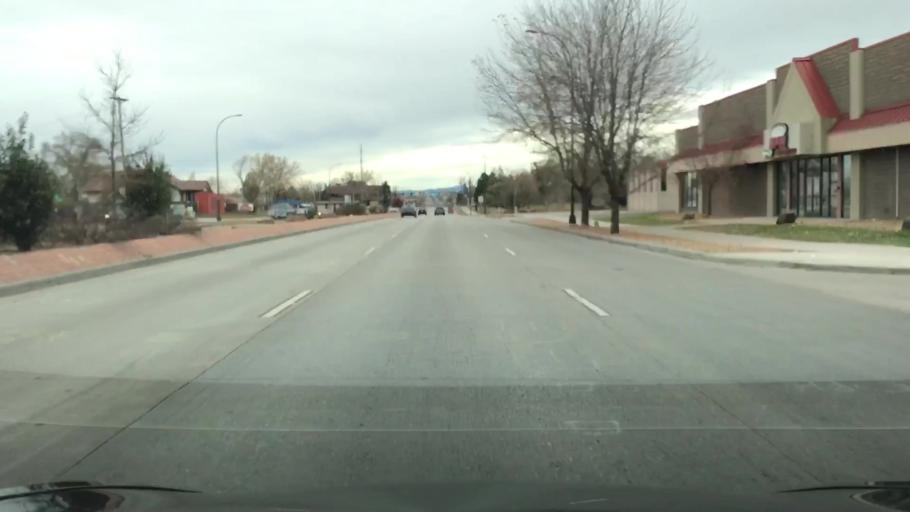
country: US
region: Colorado
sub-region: Jefferson County
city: Edgewater
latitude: 39.7366
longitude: -105.0815
